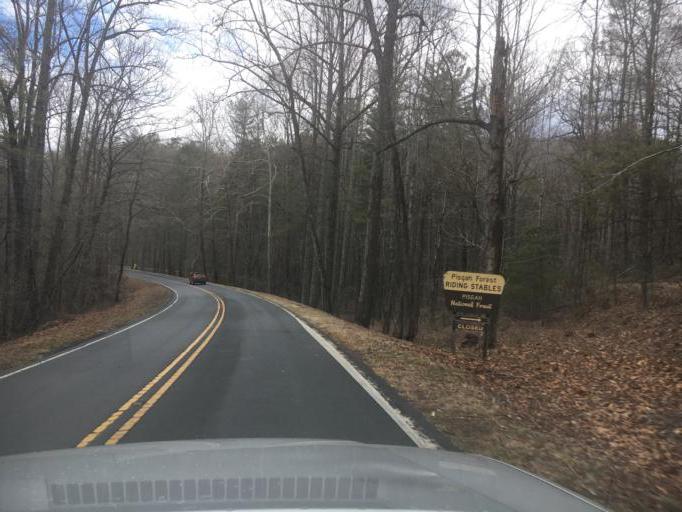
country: US
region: North Carolina
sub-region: Transylvania County
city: Brevard
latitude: 35.2879
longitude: -82.7347
